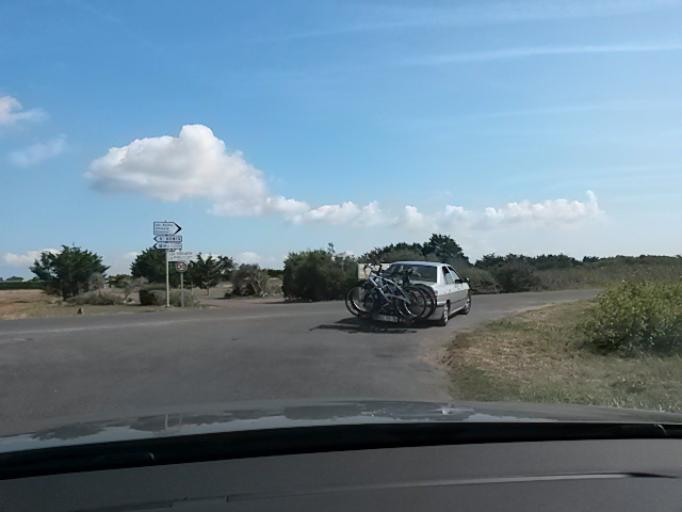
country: FR
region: Poitou-Charentes
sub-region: Departement de la Charente-Maritime
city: Saint-Denis-d'Oleron
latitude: 46.0187
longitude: -1.3920
